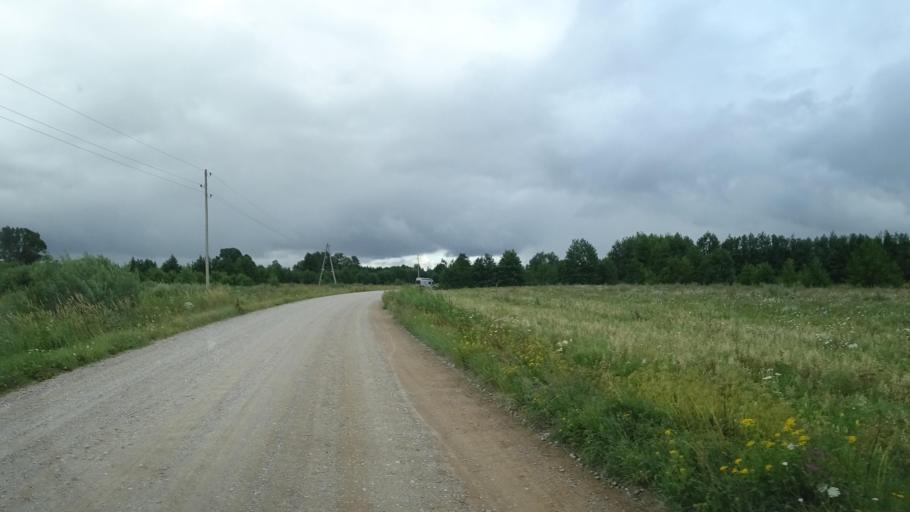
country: LV
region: Liepaja
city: Vec-Liepaja
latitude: 56.6301
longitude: 21.0494
